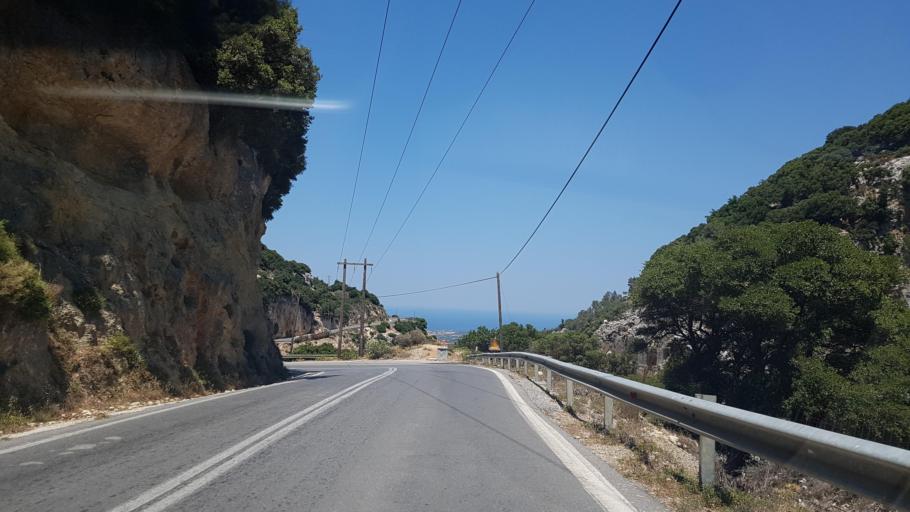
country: GR
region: Crete
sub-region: Nomos Rethymnis
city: Agia Foteini
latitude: 35.3136
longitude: 24.6262
